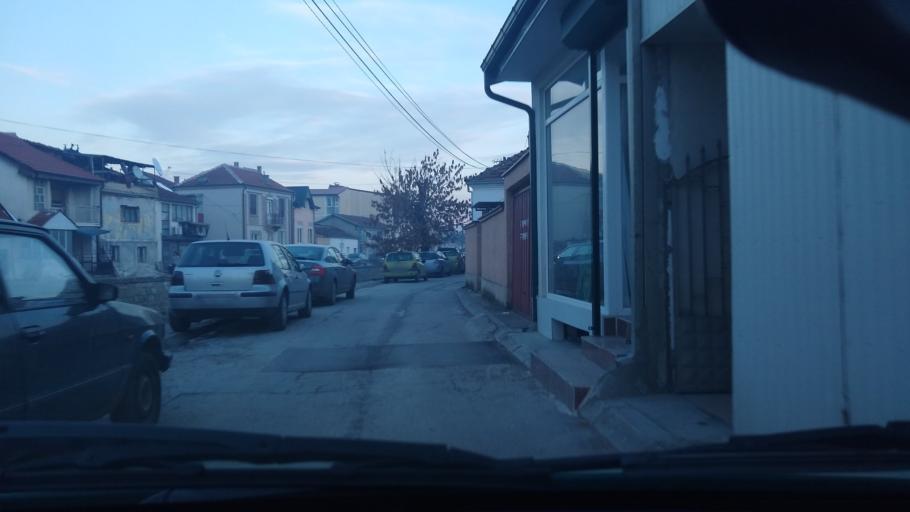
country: MK
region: Bitola
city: Bitola
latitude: 41.0316
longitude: 21.3401
